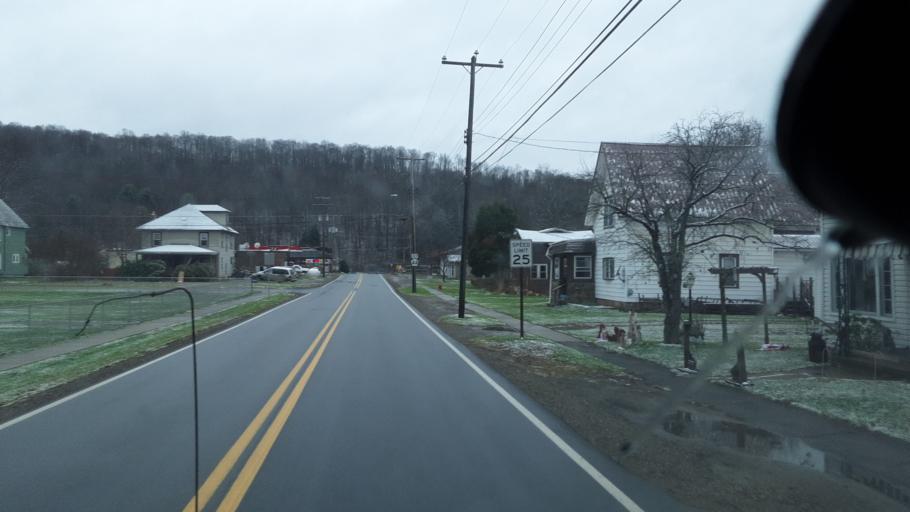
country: US
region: Pennsylvania
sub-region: Potter County
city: Shinglehouse
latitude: 41.9634
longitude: -78.1968
